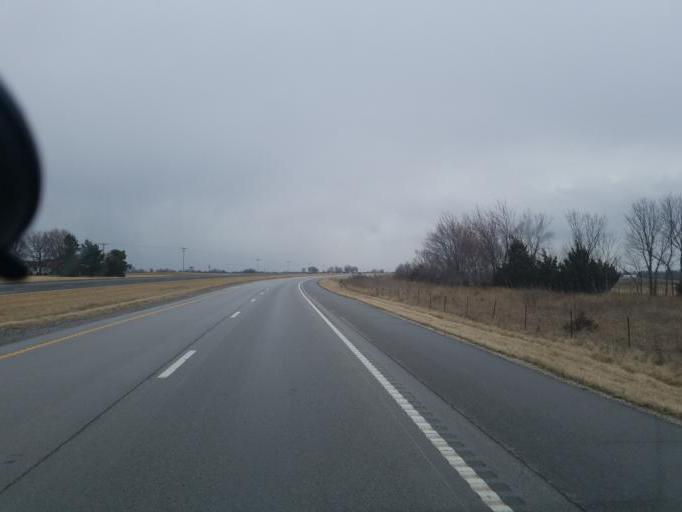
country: US
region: Missouri
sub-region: Macon County
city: Macon
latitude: 39.8333
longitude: -92.4759
